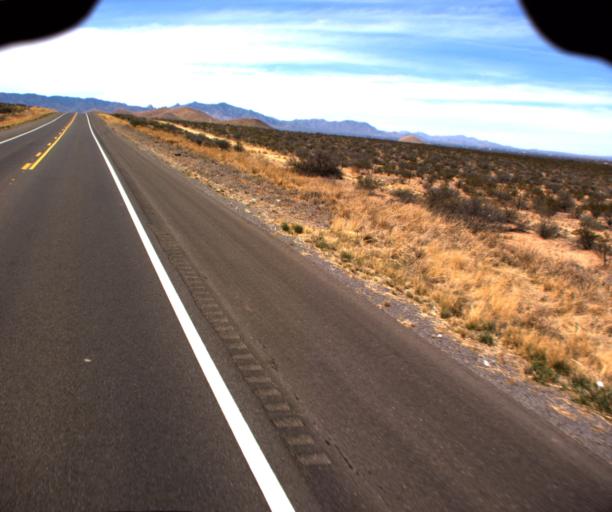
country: US
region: Arizona
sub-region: Cochise County
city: Willcox
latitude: 31.9056
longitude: -109.7394
